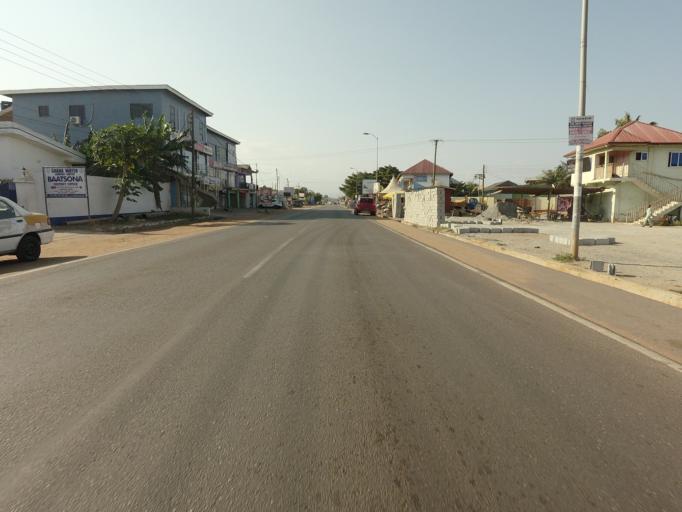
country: GH
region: Greater Accra
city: Nungua
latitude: 5.6330
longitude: -0.0762
